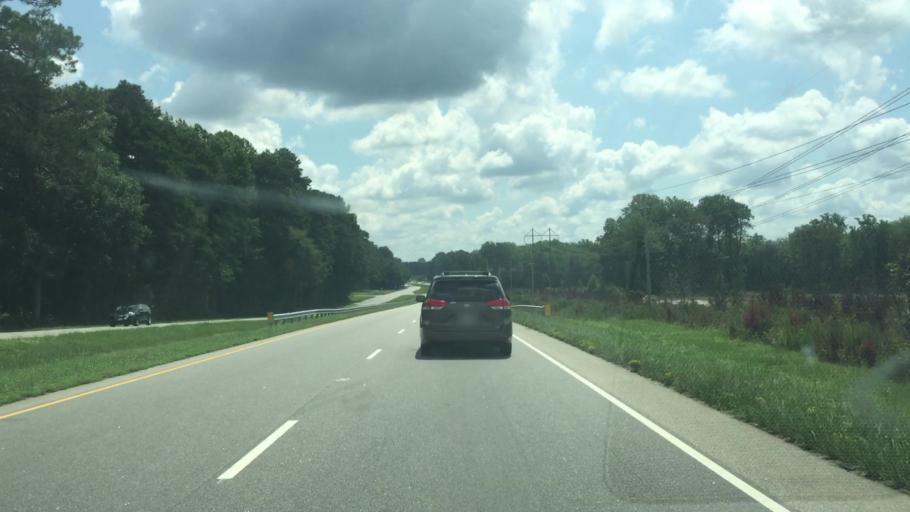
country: US
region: North Carolina
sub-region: Scotland County
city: Laurel Hill
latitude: 34.8164
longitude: -79.5711
